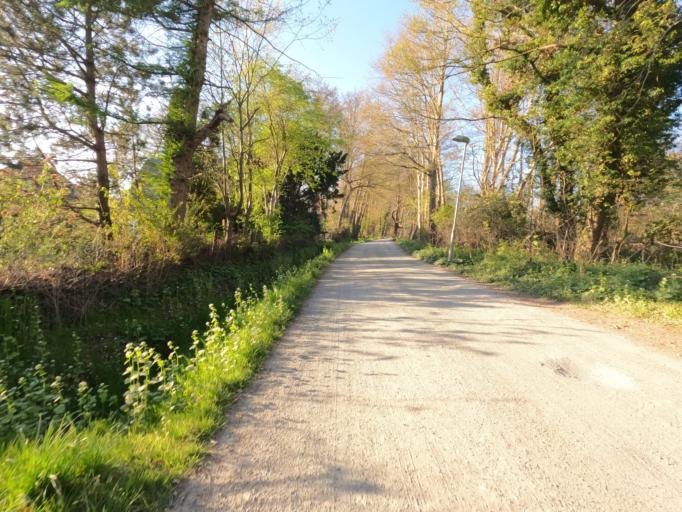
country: DE
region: Mecklenburg-Vorpommern
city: Ostseebad Prerow
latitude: 54.4419
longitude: 12.5518
